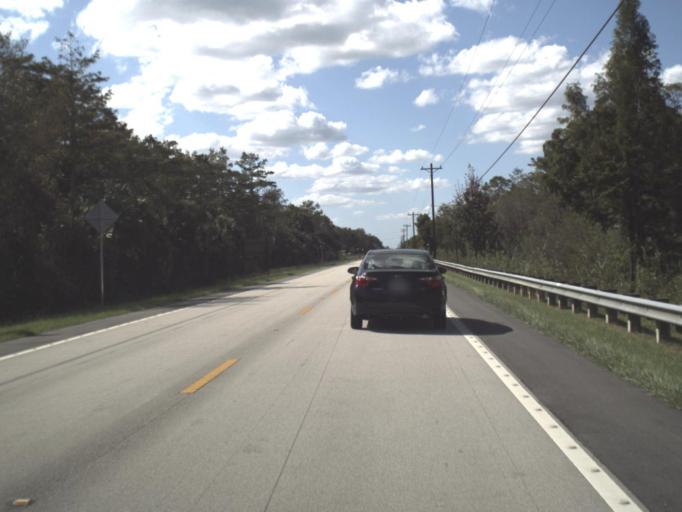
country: US
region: Florida
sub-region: Collier County
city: Marco
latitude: 25.8929
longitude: -81.2744
